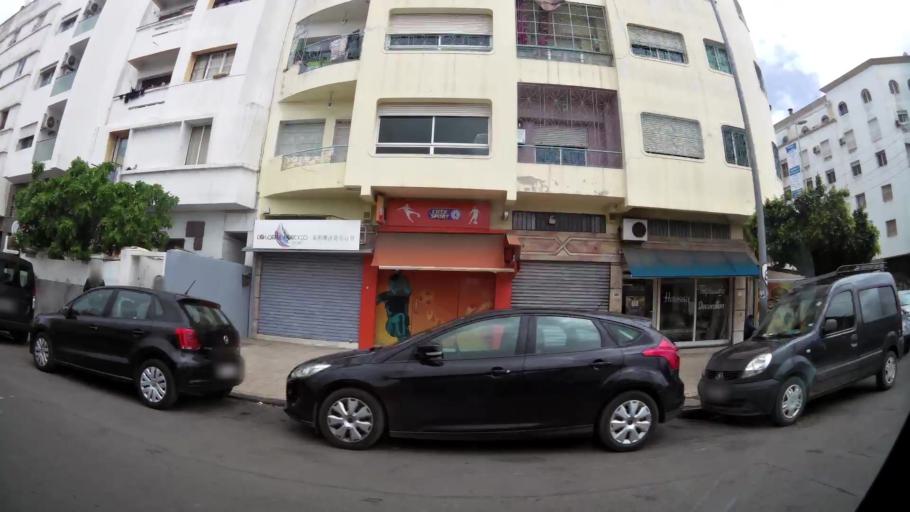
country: MA
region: Grand Casablanca
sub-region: Casablanca
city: Casablanca
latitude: 33.5961
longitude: -7.6423
